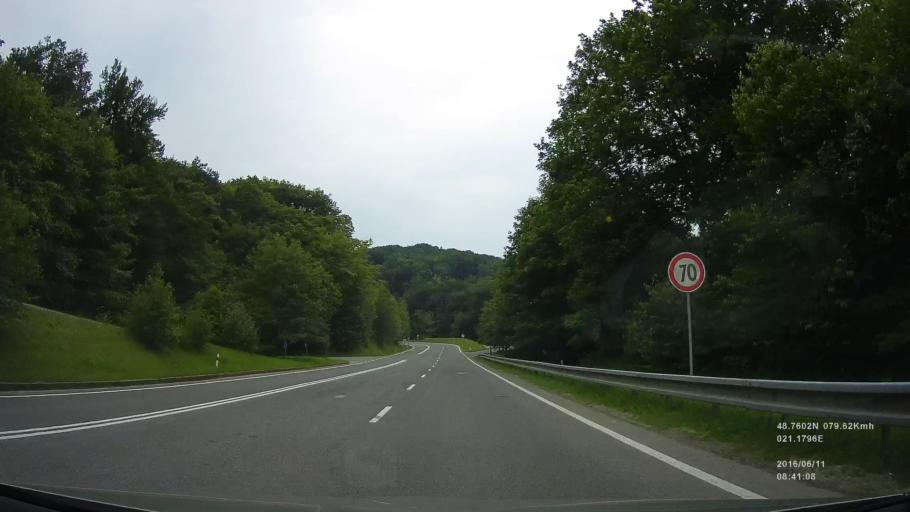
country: SK
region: Kosicky
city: Kosice
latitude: 48.7503
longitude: 21.2269
